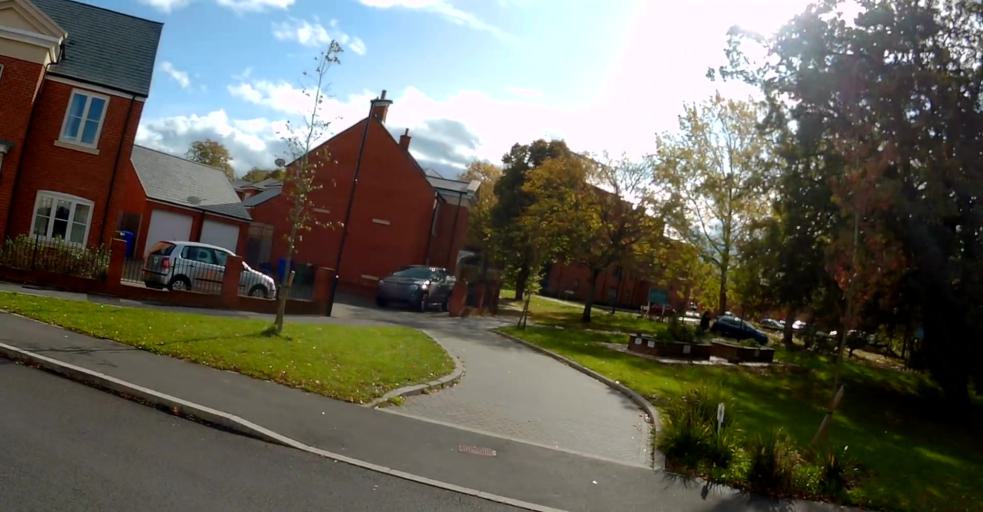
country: GB
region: England
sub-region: Hampshire
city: Aldershot
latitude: 51.2550
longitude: -0.7628
